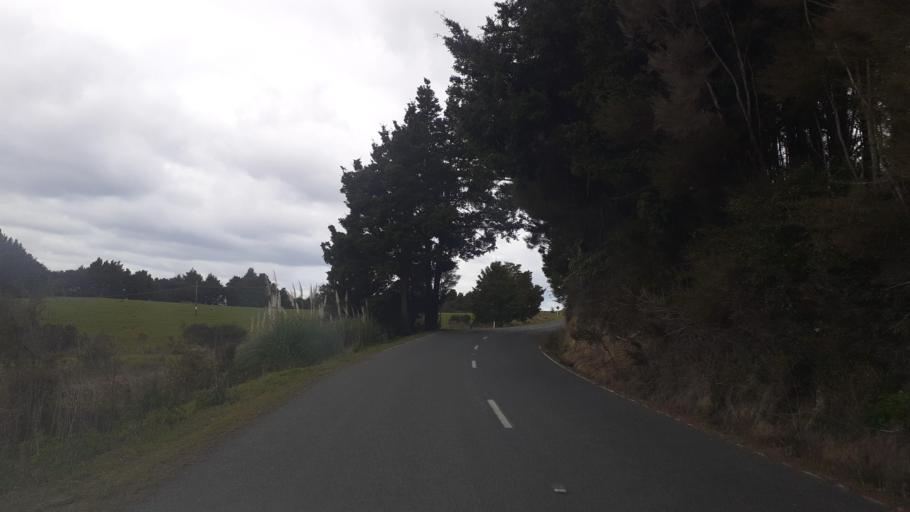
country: NZ
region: Northland
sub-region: Far North District
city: Moerewa
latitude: -35.5888
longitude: 173.9739
